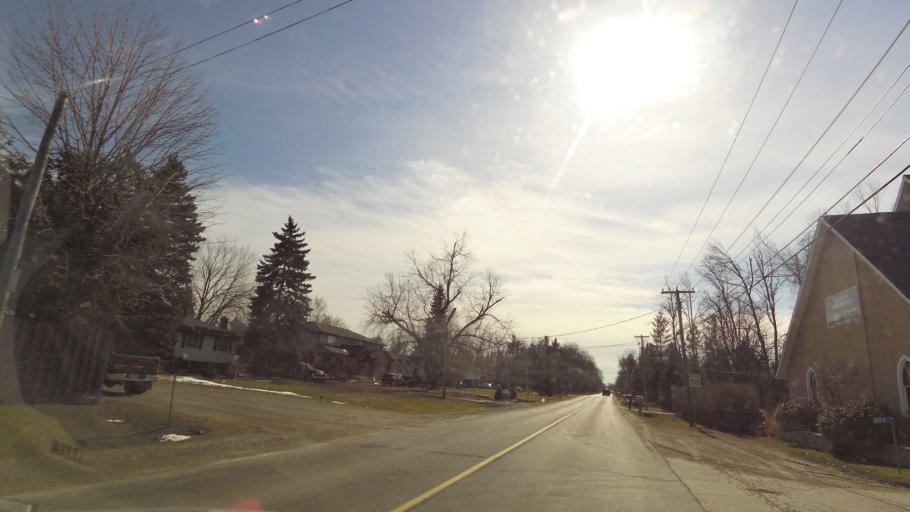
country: CA
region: Ontario
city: Burlington
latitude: 43.3598
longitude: -79.9355
